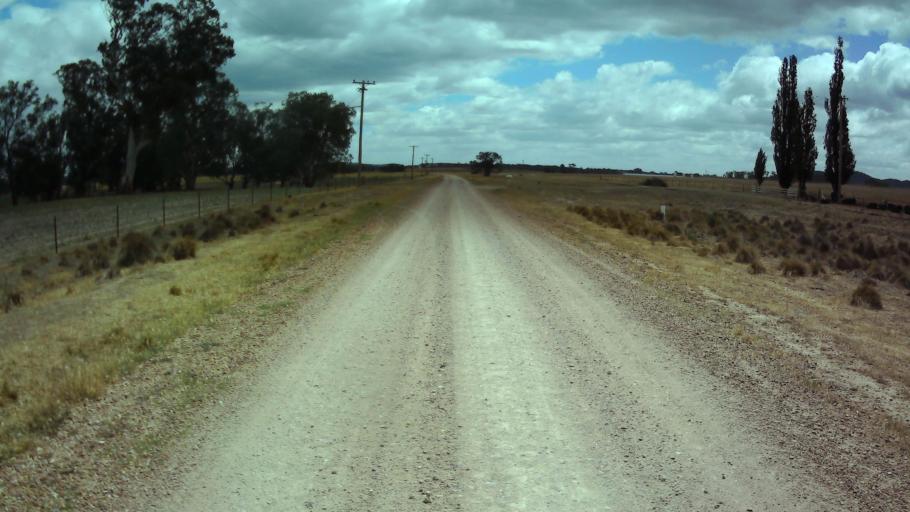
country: AU
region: New South Wales
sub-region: Weddin
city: Grenfell
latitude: -33.9415
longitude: 148.2900
